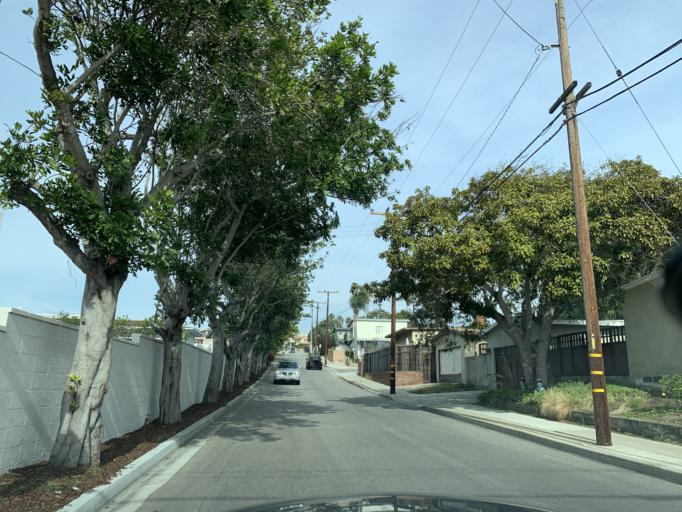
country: US
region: California
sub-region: Los Angeles County
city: Hermosa Beach
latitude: 33.8743
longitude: -118.3948
